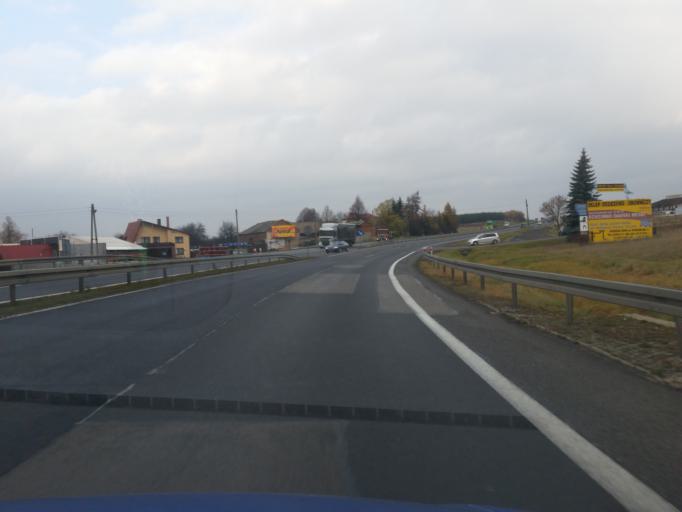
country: PL
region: Silesian Voivodeship
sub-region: Powiat myszkowski
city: Kozieglowy
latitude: 50.5760
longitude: 19.1632
